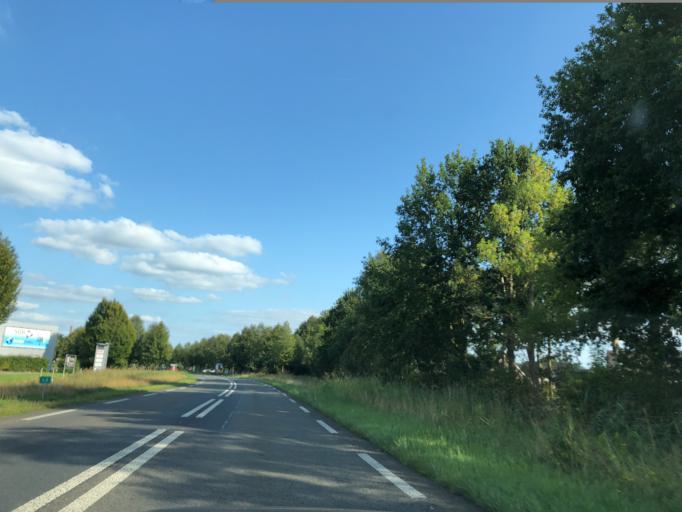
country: NL
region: Groningen
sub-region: Gemeente Stadskanaal
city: Stadskanaal
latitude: 52.9756
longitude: 6.9503
